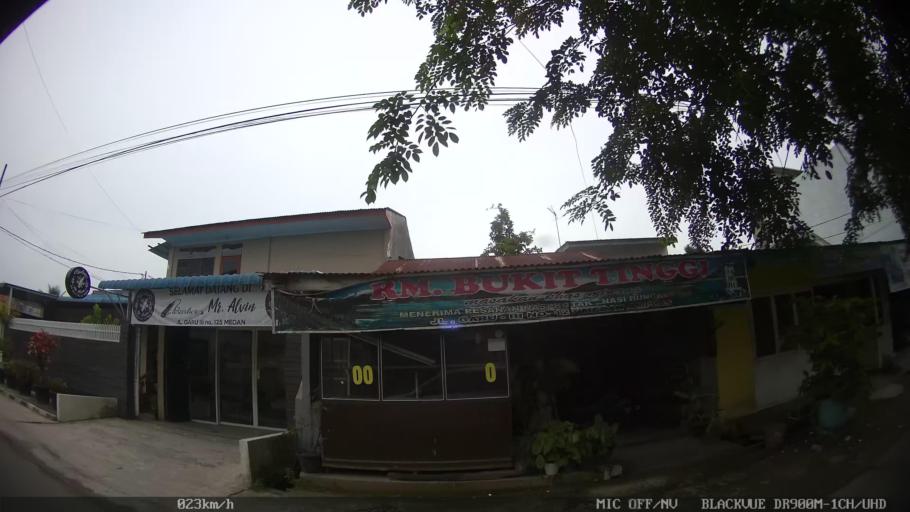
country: ID
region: North Sumatra
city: Deli Tua
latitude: 3.5432
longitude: 98.7088
